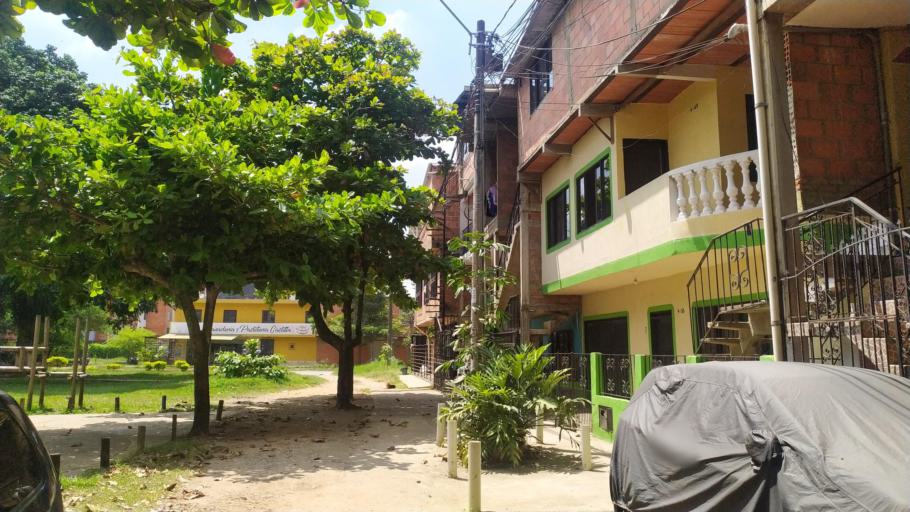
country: CO
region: Valle del Cauca
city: Jamundi
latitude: 3.2499
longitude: -76.5424
